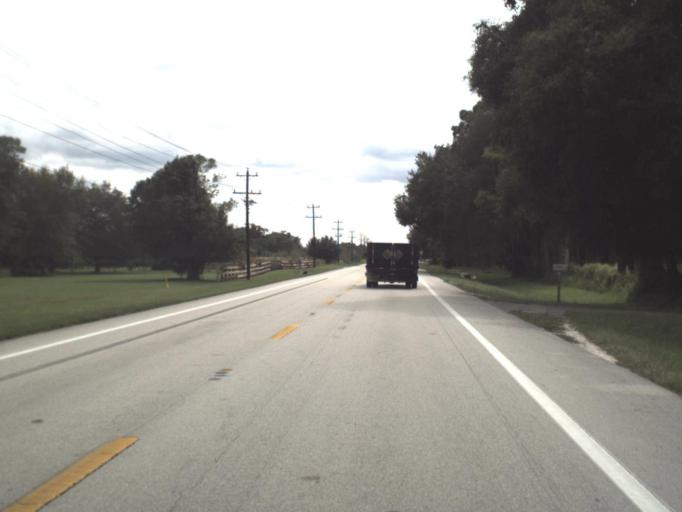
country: US
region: Florida
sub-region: Lee County
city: Fort Myers Shores
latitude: 26.7298
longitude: -81.7610
